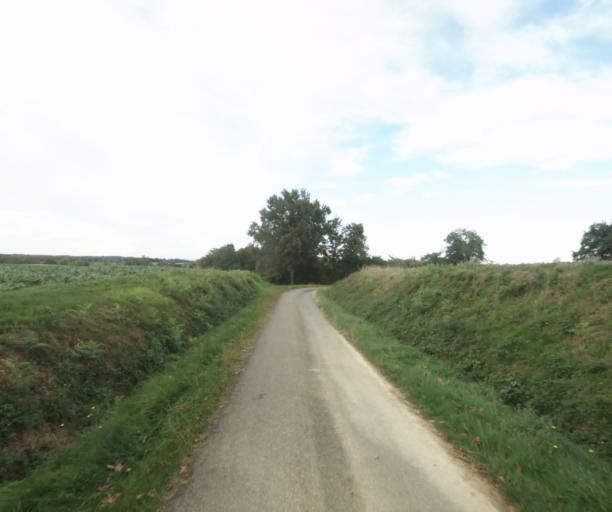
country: FR
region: Midi-Pyrenees
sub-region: Departement du Gers
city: Cazaubon
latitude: 43.8553
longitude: -0.1194
